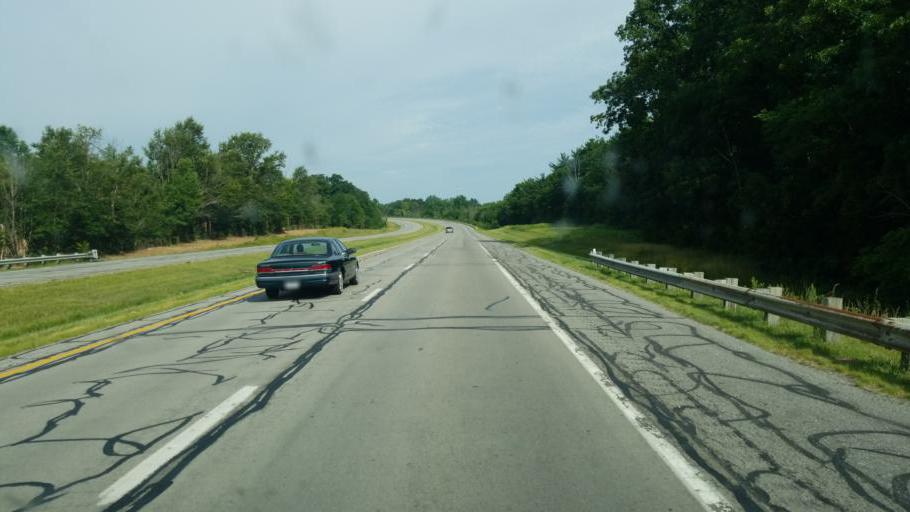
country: US
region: Ohio
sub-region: Medina County
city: Westfield Center
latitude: 41.0360
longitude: -81.9183
